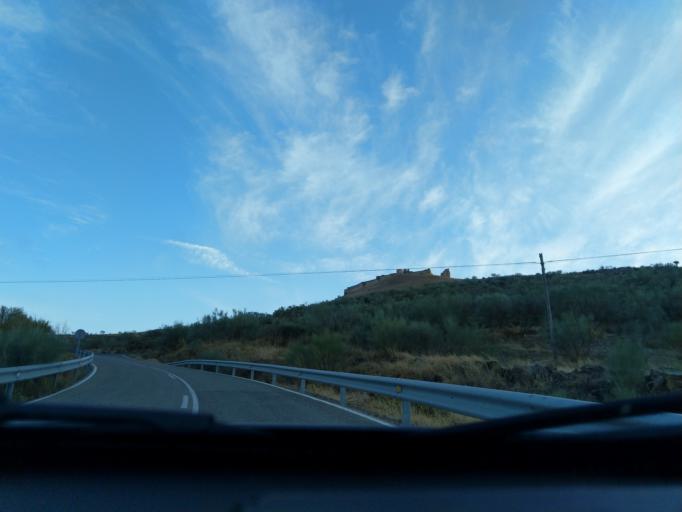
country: ES
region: Extremadura
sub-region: Provincia de Badajoz
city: Casas de Reina
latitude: 38.1961
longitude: -5.9565
